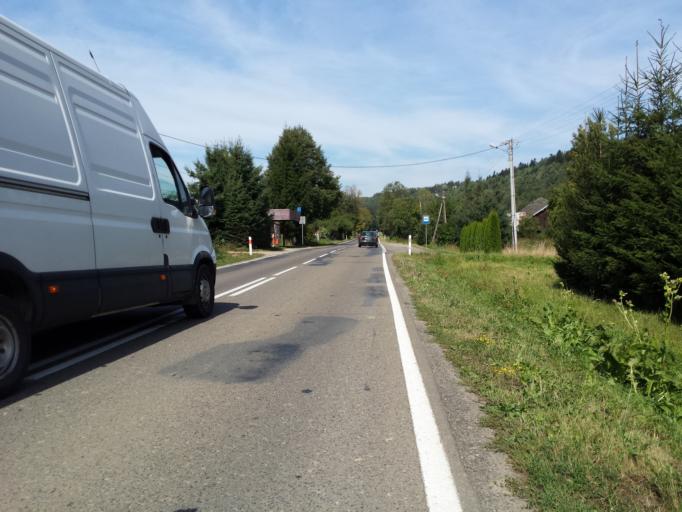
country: PL
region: Subcarpathian Voivodeship
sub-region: Powiat leski
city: Lesko
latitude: 49.4501
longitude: 22.3459
